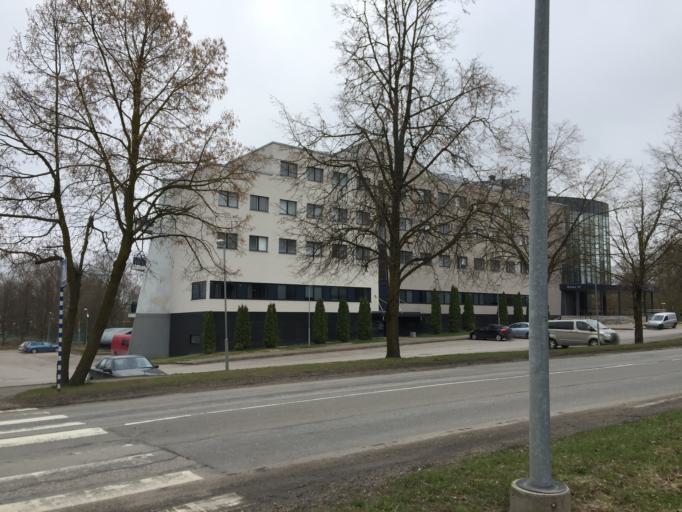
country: EE
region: Tartu
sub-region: Tartu linn
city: Tartu
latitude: 58.3684
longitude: 26.6925
